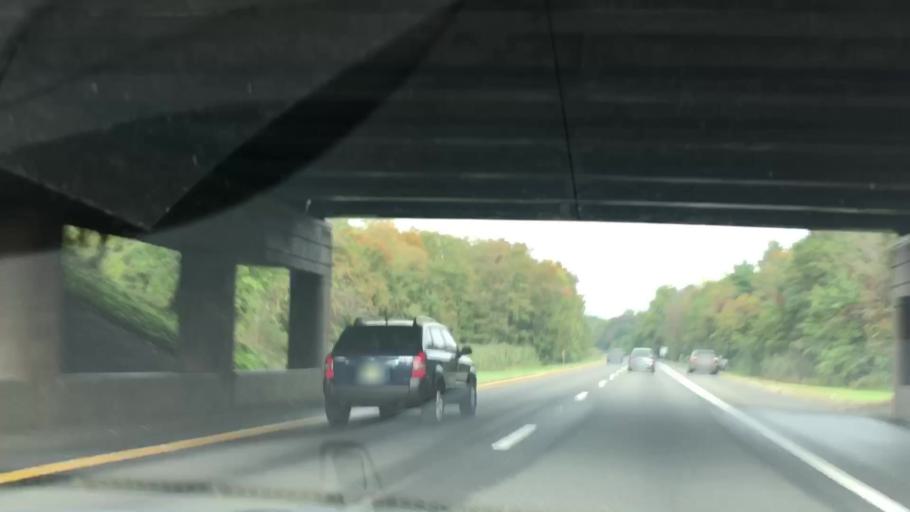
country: US
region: New Jersey
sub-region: Bergen County
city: Woodcliff Lake
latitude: 40.9987
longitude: -74.0711
